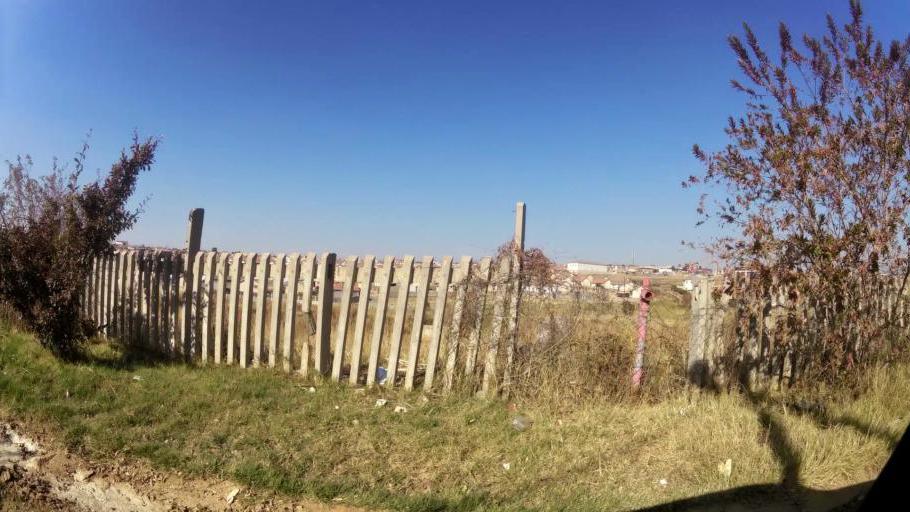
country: ZA
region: Gauteng
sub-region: West Rand District Municipality
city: Muldersdriseloop
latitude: -26.0340
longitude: 27.9191
